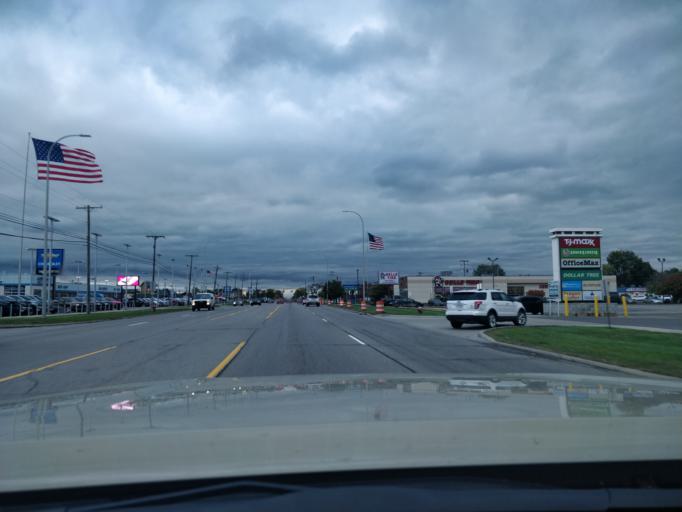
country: US
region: Michigan
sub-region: Wayne County
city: Southgate
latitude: 42.1989
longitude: -83.2143
